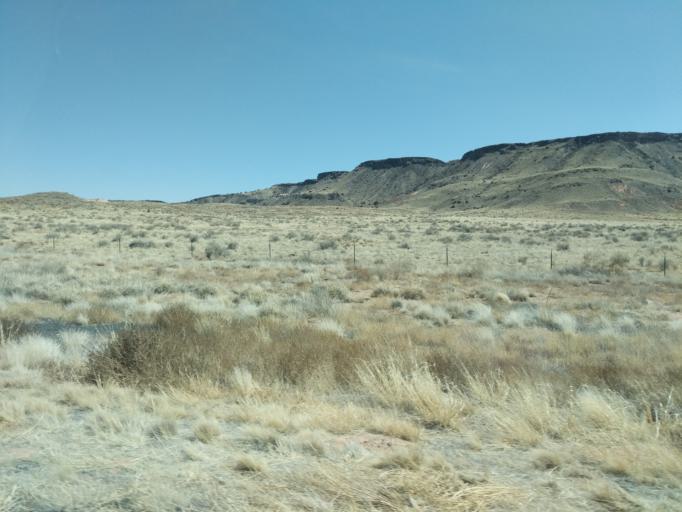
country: US
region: Arizona
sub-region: Navajo County
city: Dilkon
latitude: 35.4405
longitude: -110.0659
